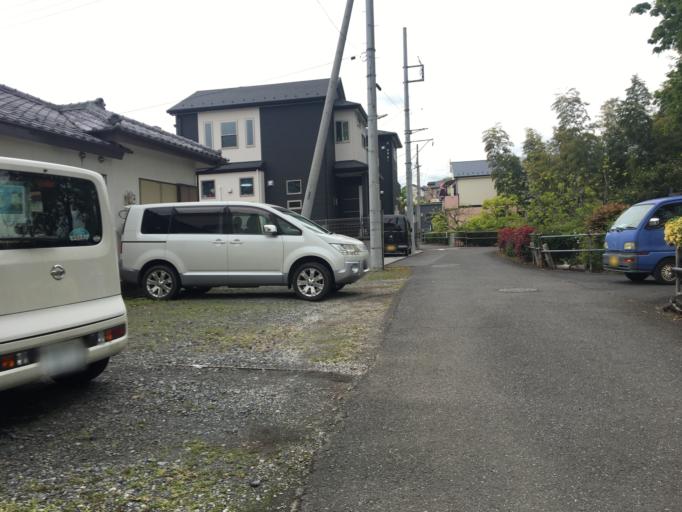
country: JP
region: Saitama
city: Oi
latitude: 35.8544
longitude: 139.5497
